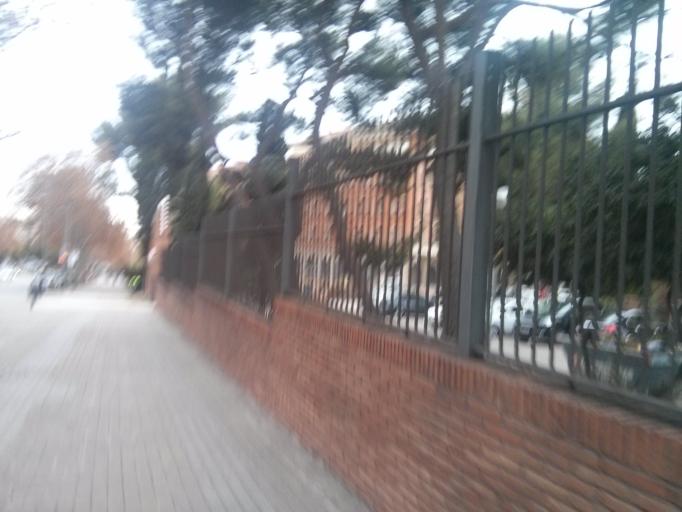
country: ES
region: Catalonia
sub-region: Provincia de Barcelona
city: les Corts
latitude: 41.3864
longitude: 2.1225
